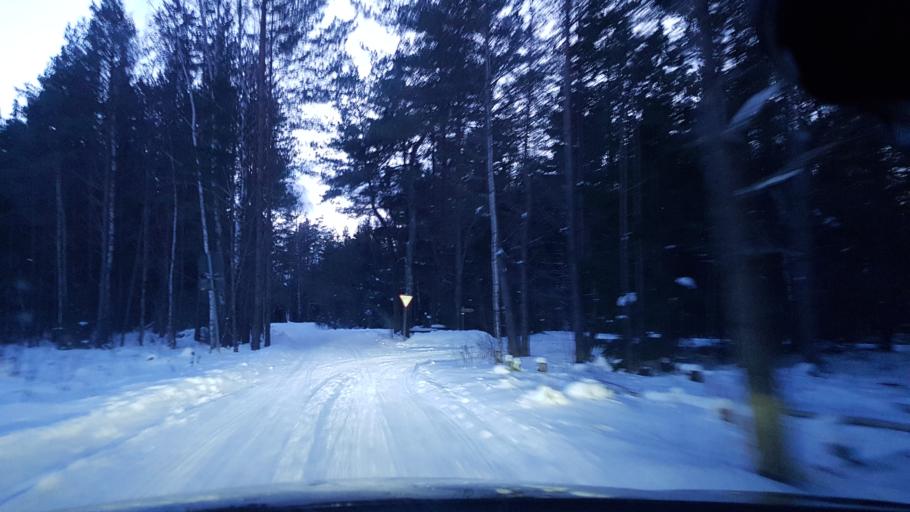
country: EE
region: Laeaene
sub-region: Haapsalu linn
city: Haapsalu
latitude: 59.2095
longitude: 23.5363
